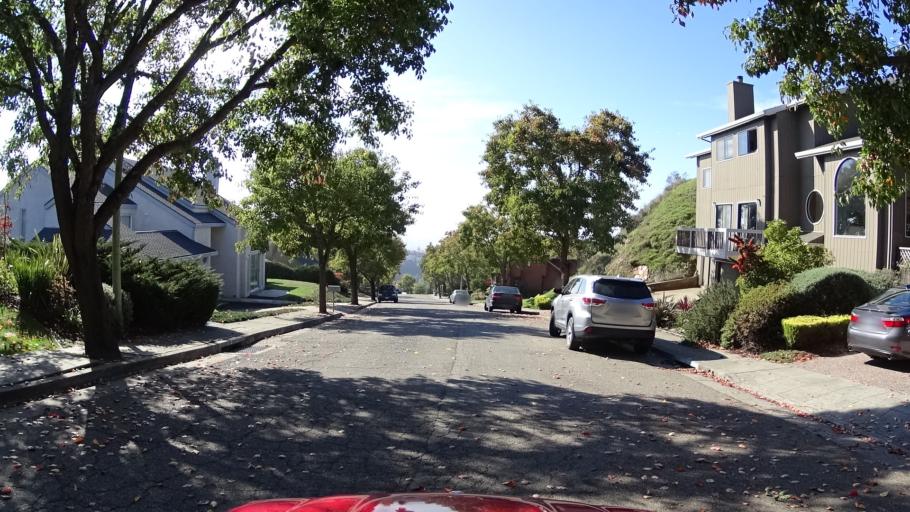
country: US
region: California
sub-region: Alameda County
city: Piedmont
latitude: 37.8463
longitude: -122.2206
